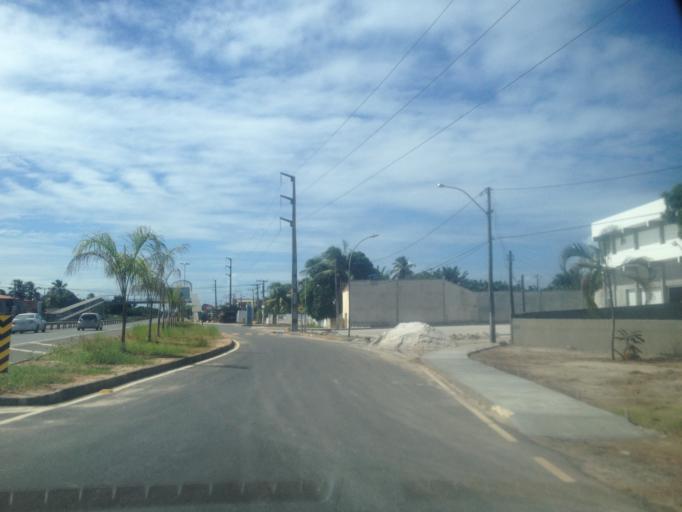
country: BR
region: Bahia
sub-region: Camacari
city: Camacari
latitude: -12.7039
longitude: -38.1346
